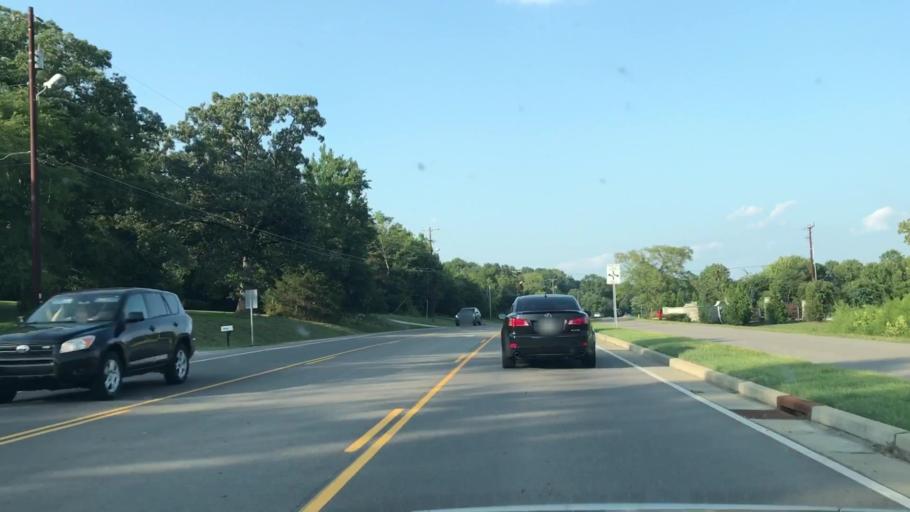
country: US
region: Tennessee
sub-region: Williamson County
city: Nolensville
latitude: 35.9904
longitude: -86.7026
